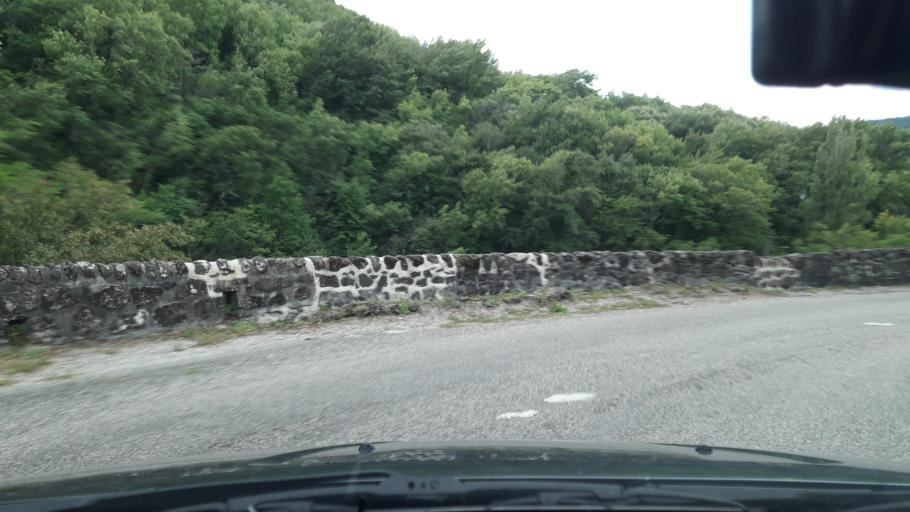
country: FR
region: Rhone-Alpes
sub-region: Departement de l'Ardeche
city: Saint-Priest
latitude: 44.6486
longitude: 4.5180
